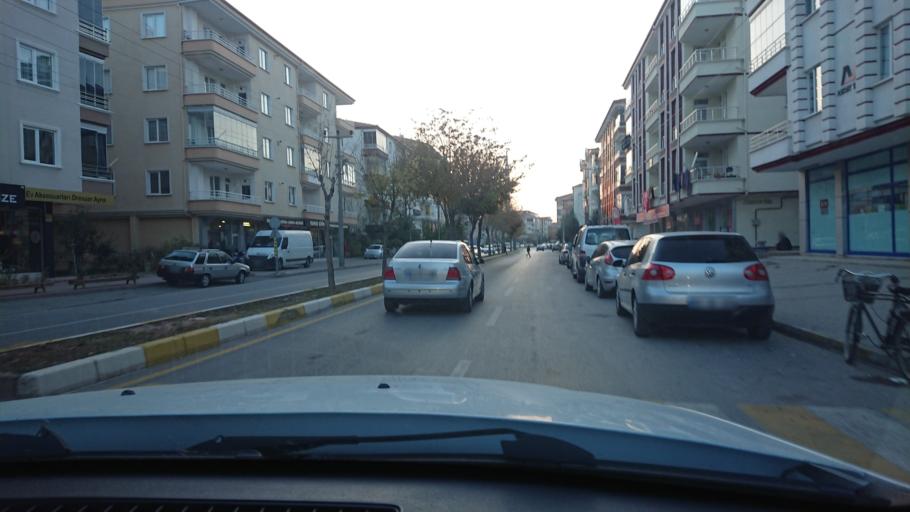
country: TR
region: Aksaray
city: Aksaray
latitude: 38.3614
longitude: 34.0259
